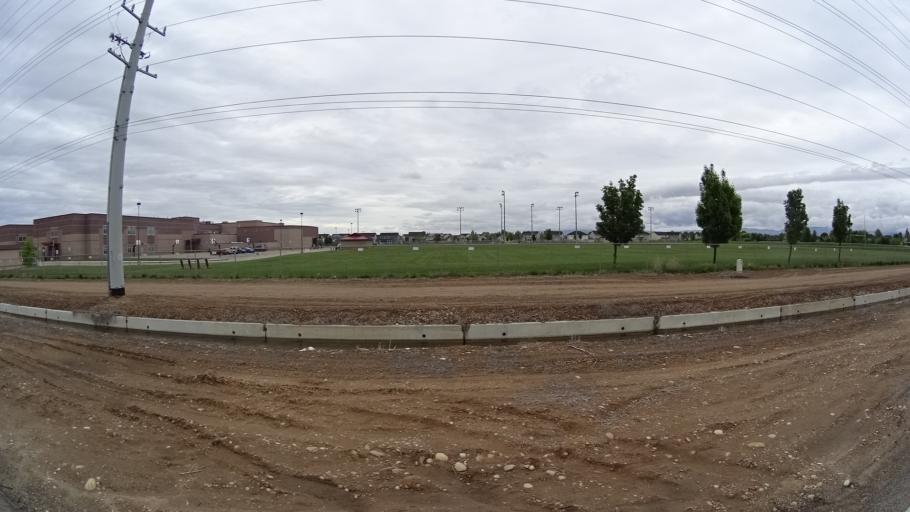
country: US
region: Idaho
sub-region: Ada County
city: Meridian
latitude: 43.6483
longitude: -116.3903
